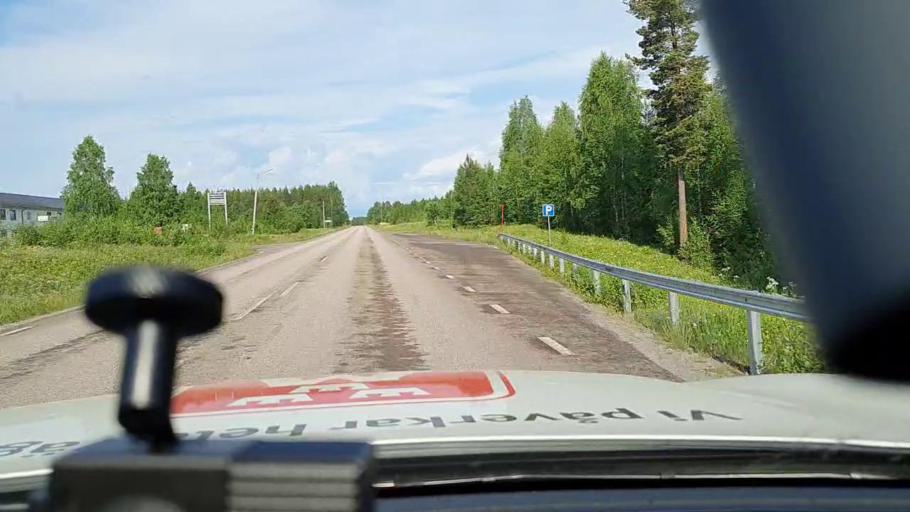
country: SE
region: Norrbotten
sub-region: Alvsbyns Kommun
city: AElvsbyn
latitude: 66.0160
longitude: 21.1578
